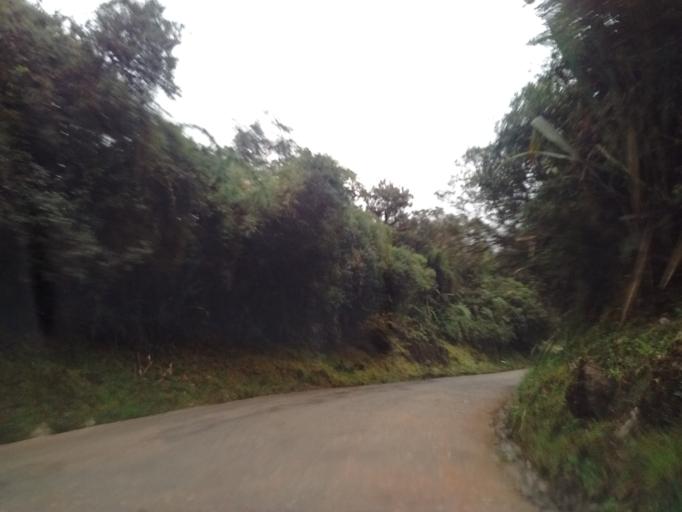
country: CO
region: Huila
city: Isnos
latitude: 2.1304
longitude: -76.3800
